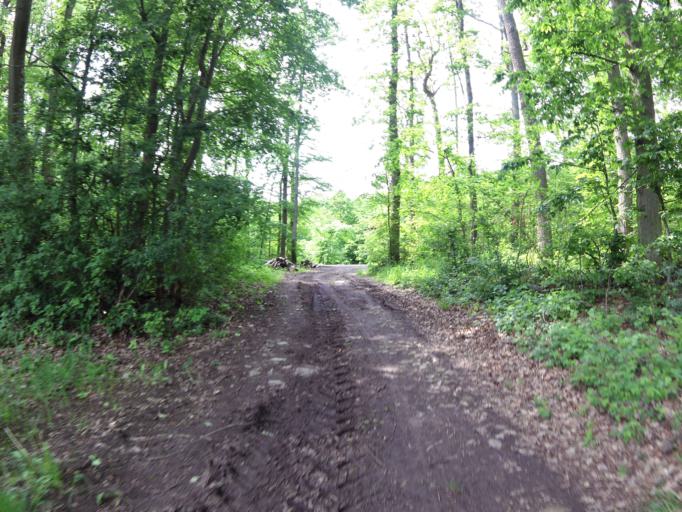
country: DE
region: Bavaria
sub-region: Regierungsbezirk Unterfranken
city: Reichenberg
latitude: 49.7324
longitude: 9.8977
